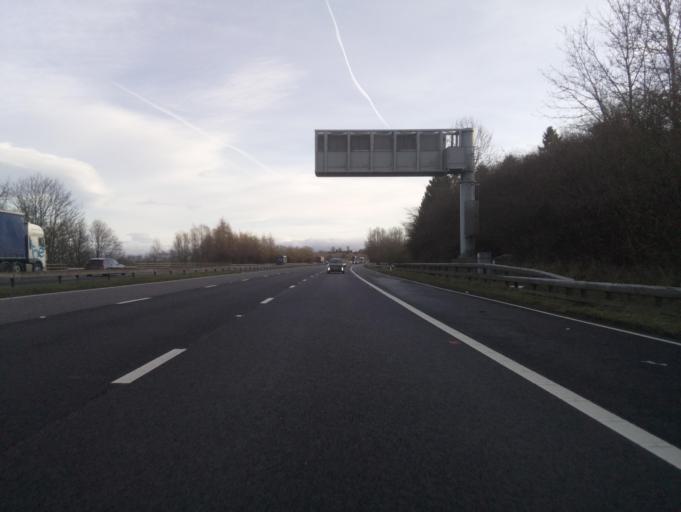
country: GB
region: England
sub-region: Cumbria
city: Penrith
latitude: 54.6435
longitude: -2.7382
